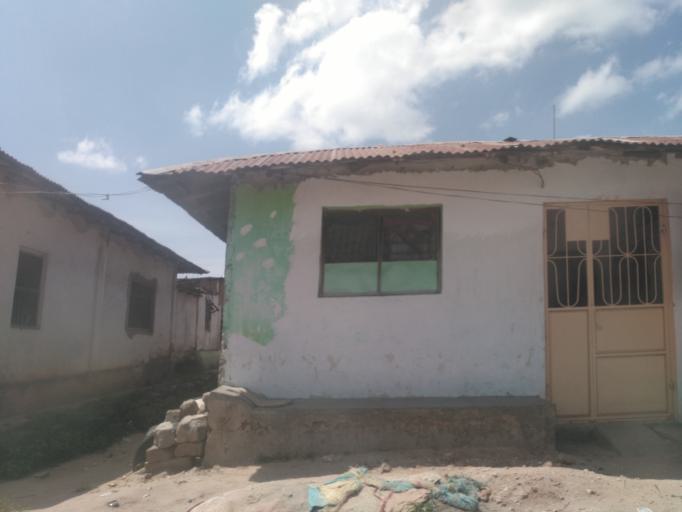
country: TZ
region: Zanzibar Urban/West
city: Zanzibar
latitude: -6.1721
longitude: 39.2092
